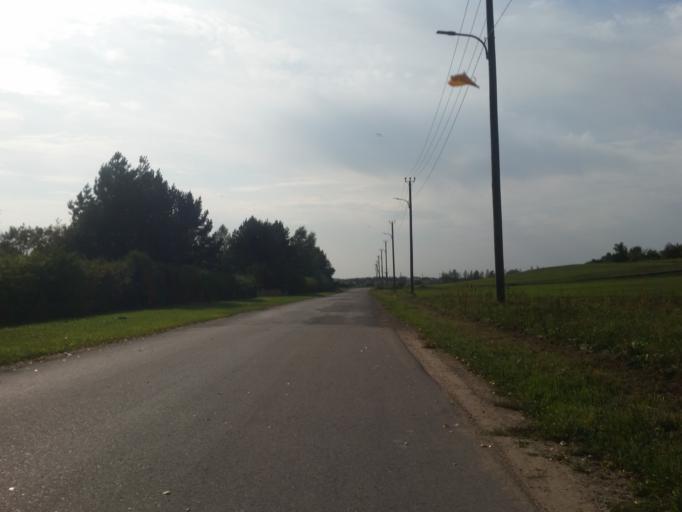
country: LV
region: Ikskile
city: Ikskile
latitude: 56.8187
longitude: 24.5255
